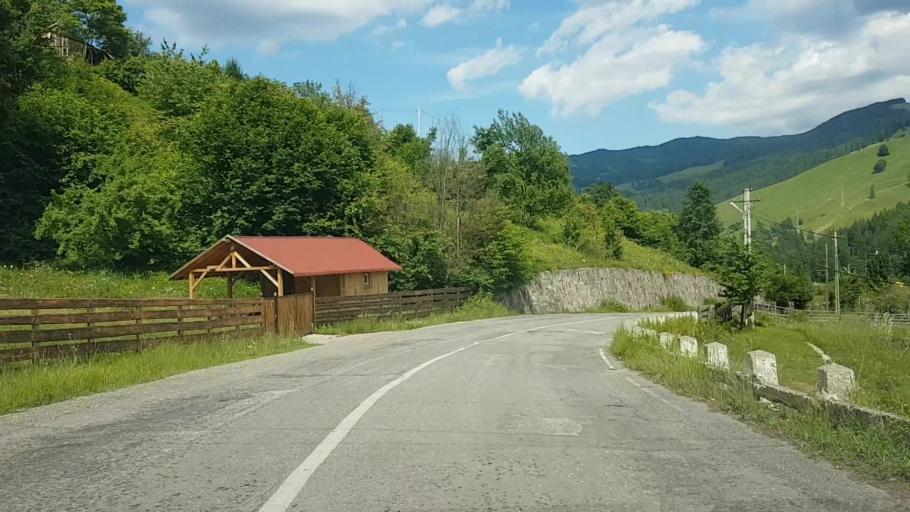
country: RO
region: Neamt
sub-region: Comuna Hangu
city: Hangu
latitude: 47.0179
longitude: 26.0758
